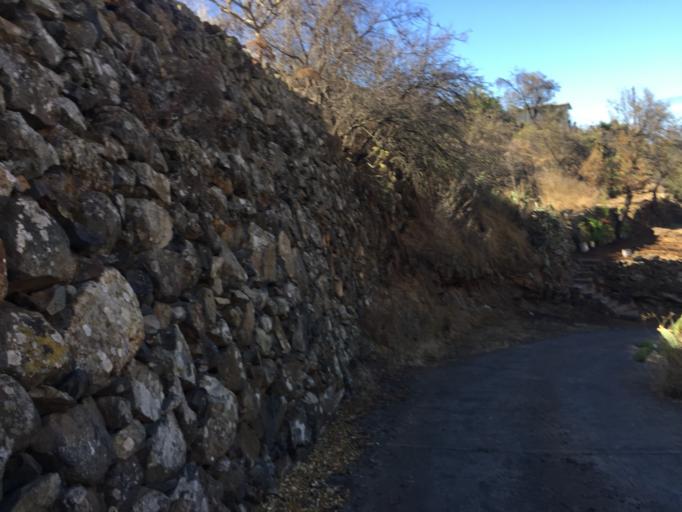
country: ES
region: Canary Islands
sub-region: Provincia de Santa Cruz de Tenerife
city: Tijarafe
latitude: 28.7230
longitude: -17.9658
